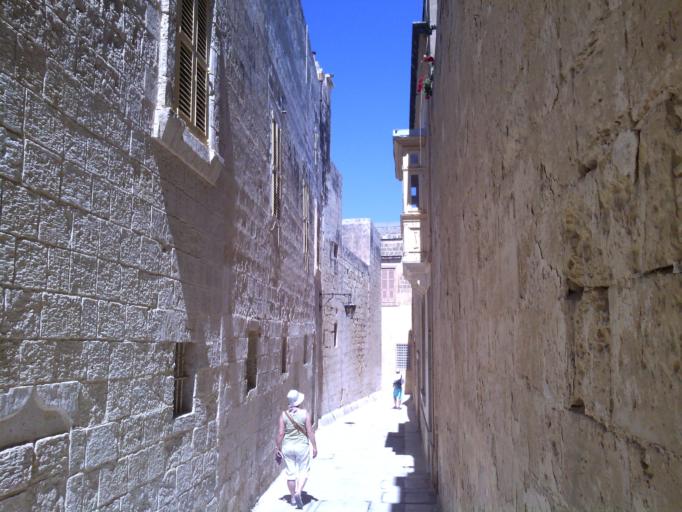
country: MT
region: L-Imdina
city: Imdina
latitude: 35.8858
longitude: 14.4024
